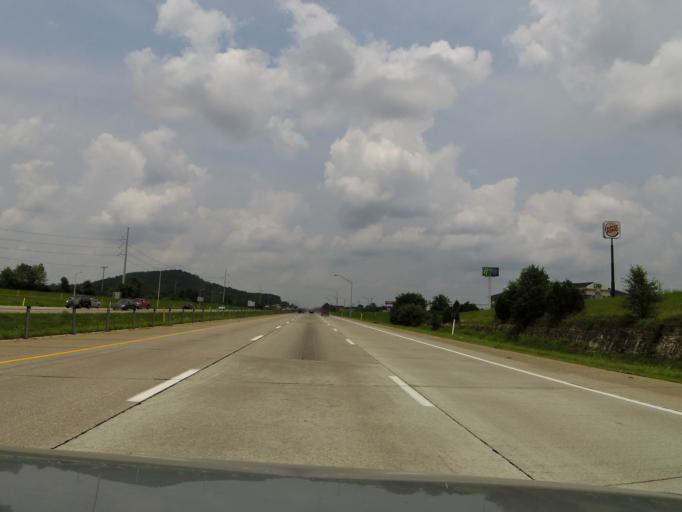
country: US
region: Kentucky
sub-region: Bullitt County
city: Brooks
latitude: 38.0643
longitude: -85.6992
